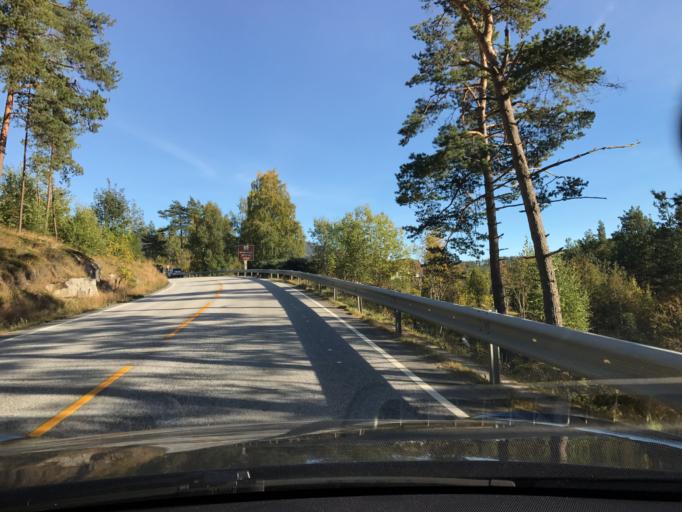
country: NO
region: Sogn og Fjordane
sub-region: Sogndal
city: Sogndalsfjora
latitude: 61.2064
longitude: 7.1690
